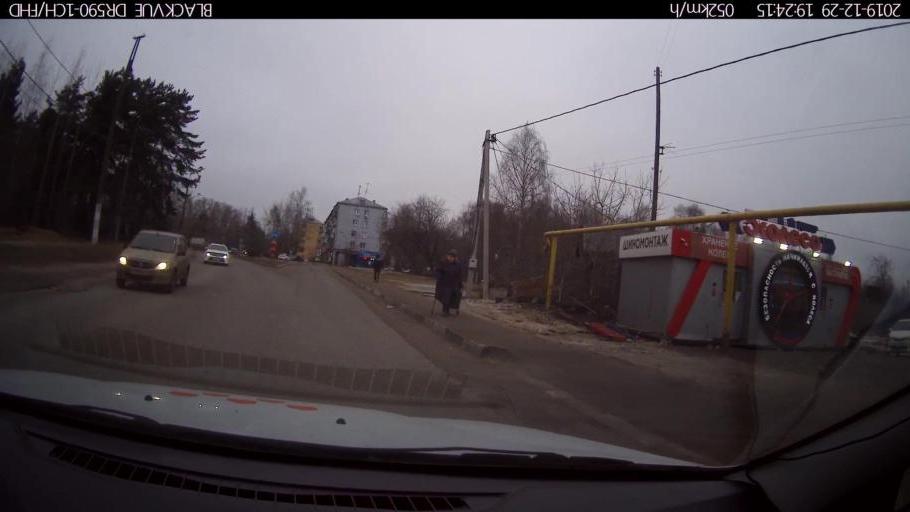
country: RU
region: Nizjnij Novgorod
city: Neklyudovo
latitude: 56.3379
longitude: 43.8672
